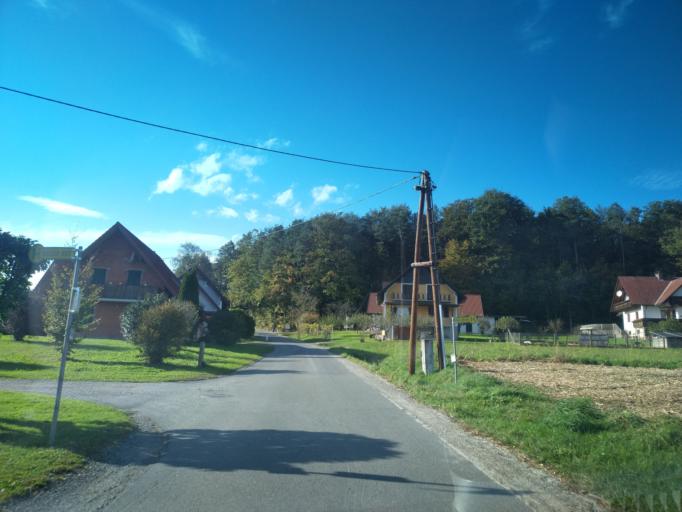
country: AT
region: Styria
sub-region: Politischer Bezirk Leibnitz
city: Sankt Johann im Saggautal
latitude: 46.7025
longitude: 15.3827
